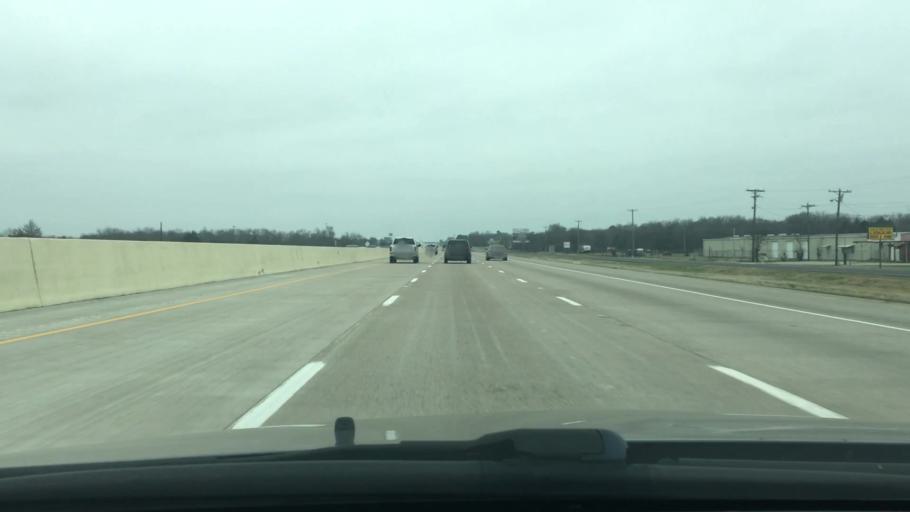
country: US
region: Texas
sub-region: Navarro County
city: Corsicana
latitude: 32.0237
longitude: -96.4403
